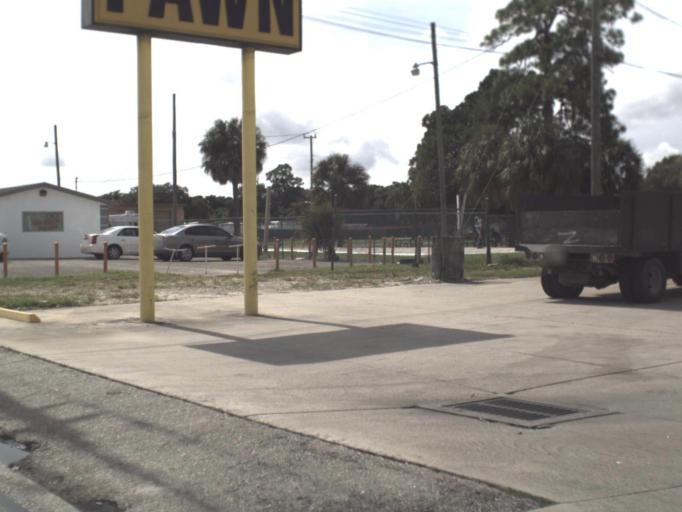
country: US
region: Florida
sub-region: Lee County
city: Fort Myers
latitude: 26.6333
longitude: -81.8623
